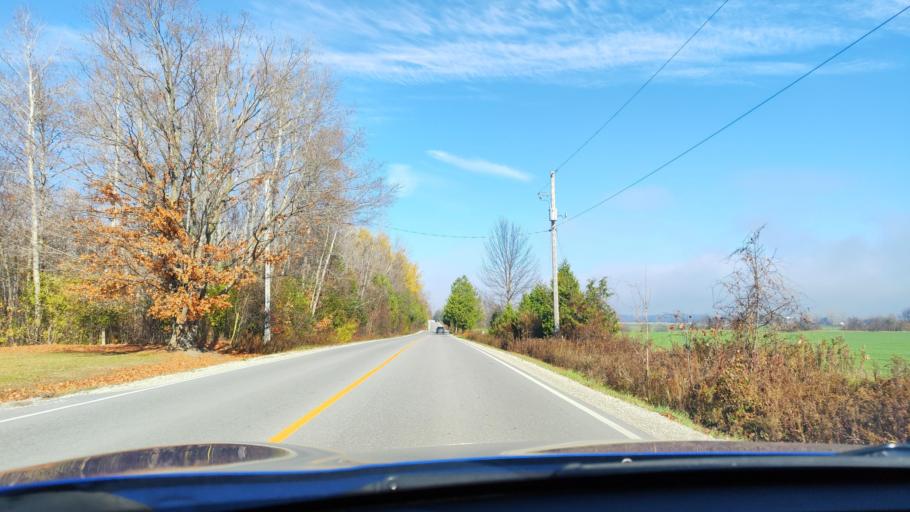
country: CA
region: Ontario
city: Wasaga Beach
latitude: 44.4138
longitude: -80.0609
